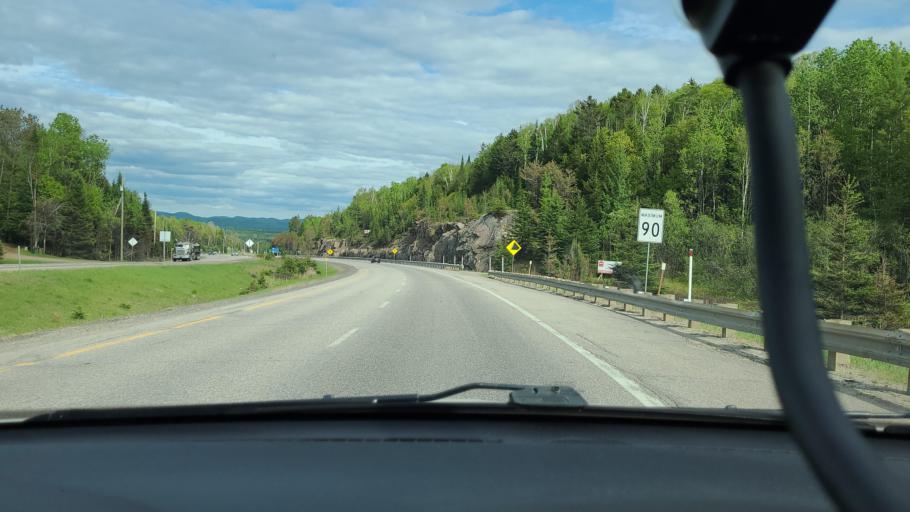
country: CA
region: Quebec
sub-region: Laurentides
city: Mont-Tremblant
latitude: 46.1356
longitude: -74.6287
